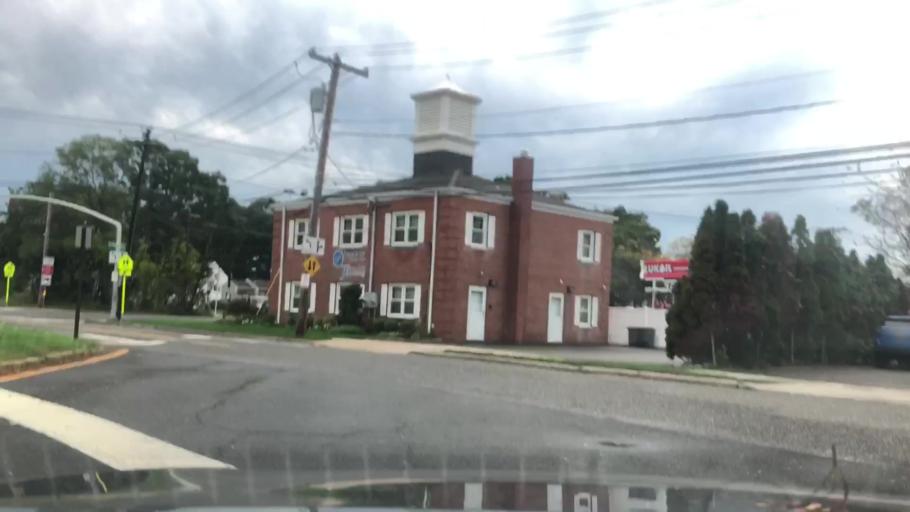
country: US
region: New York
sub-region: Nassau County
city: North Massapequa
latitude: 40.7049
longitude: -73.4622
